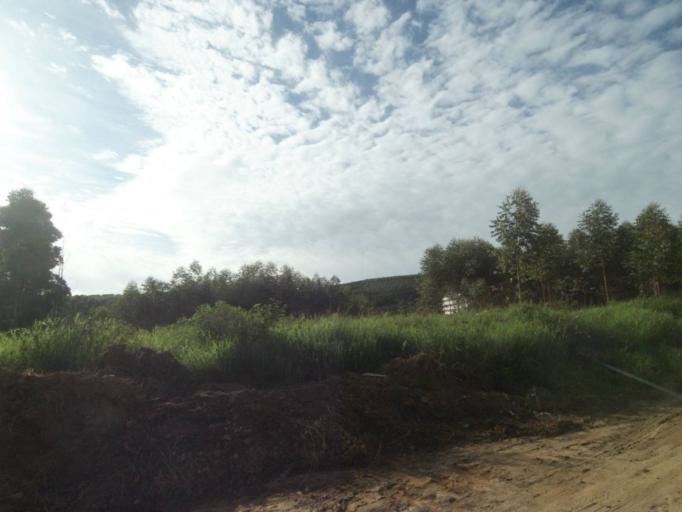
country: BR
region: Parana
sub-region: Telemaco Borba
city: Telemaco Borba
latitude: -24.3487
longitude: -50.6131
